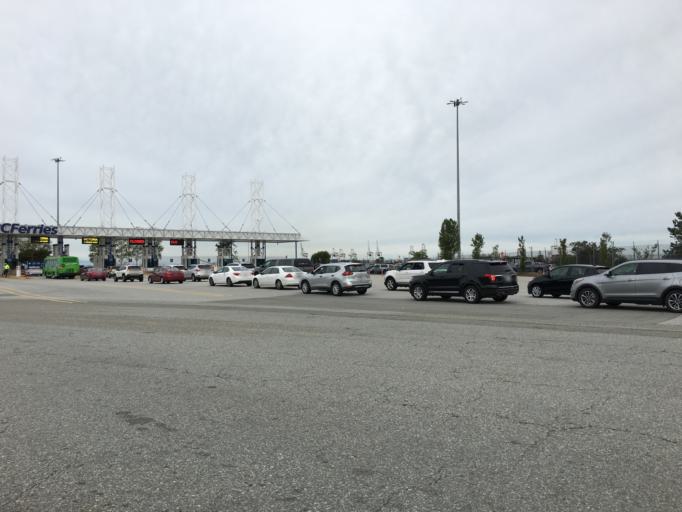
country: US
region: Washington
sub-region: Whatcom County
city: Point Roberts
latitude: 49.0107
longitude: -123.1250
